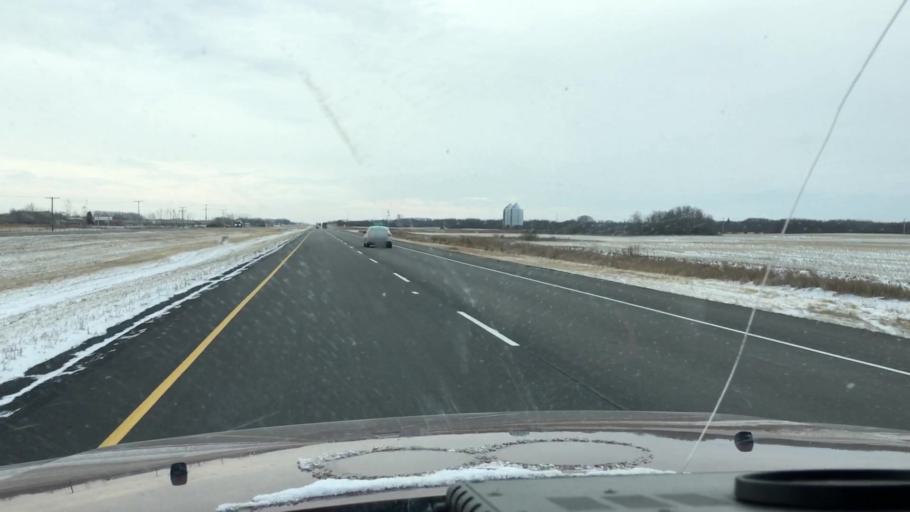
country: CA
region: Saskatchewan
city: Saskatoon
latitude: 52.0022
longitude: -106.5691
